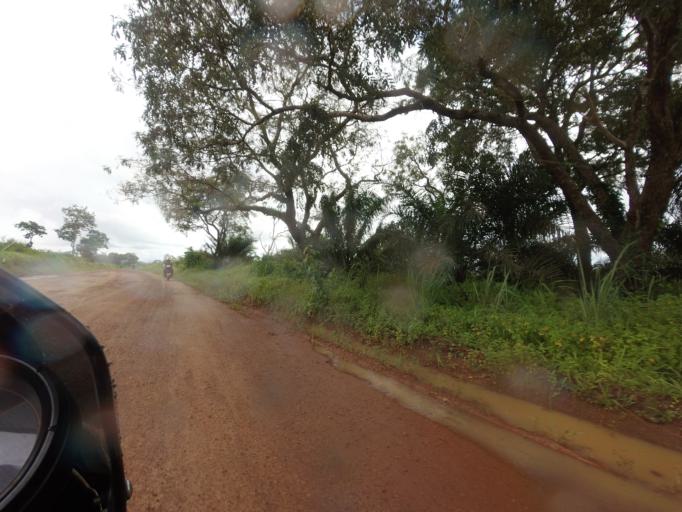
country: SL
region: Northern Province
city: Kukuna
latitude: 9.2729
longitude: -12.6874
